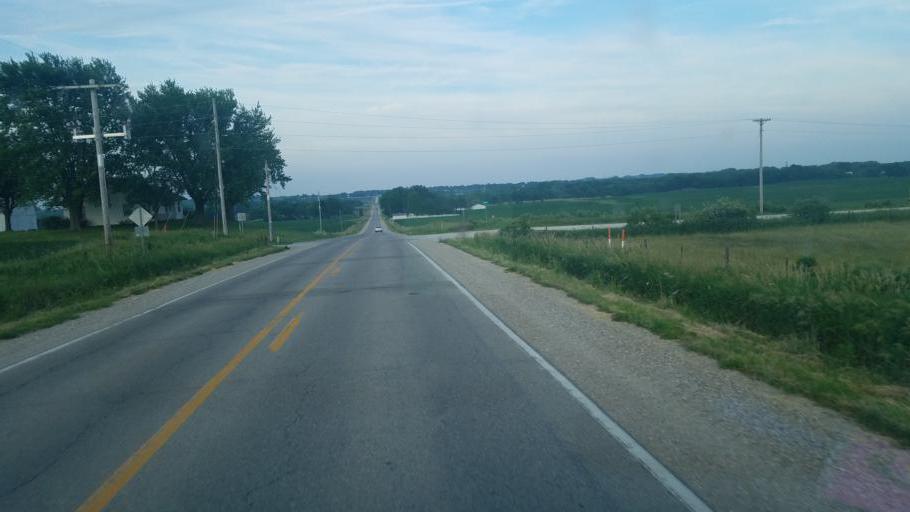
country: US
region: Iowa
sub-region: Benton County
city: Belle Plaine
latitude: 41.9061
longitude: -92.3184
